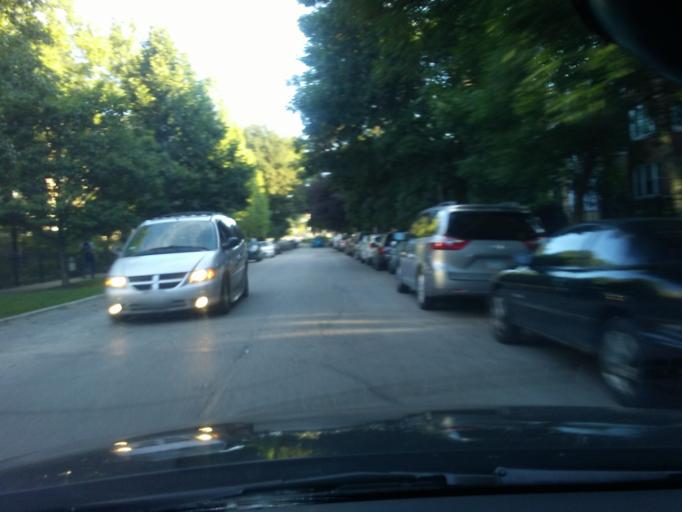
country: US
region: Illinois
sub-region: Cook County
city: Lincolnwood
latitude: 41.9676
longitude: -87.6642
